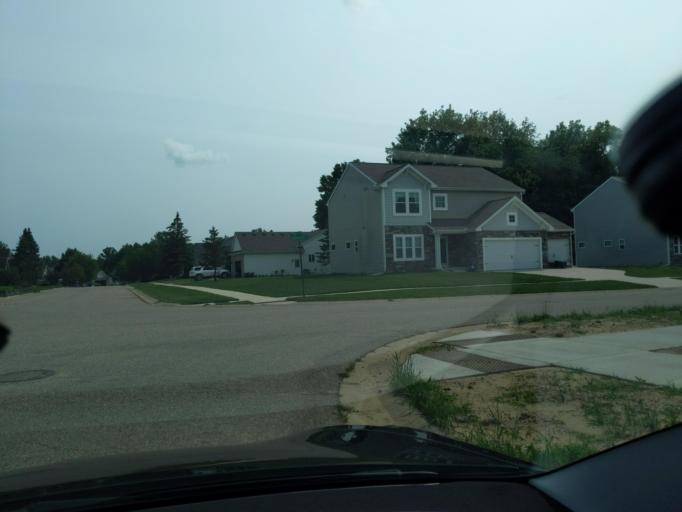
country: US
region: Michigan
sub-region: Ingham County
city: Holt
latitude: 42.6301
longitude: -84.5560
